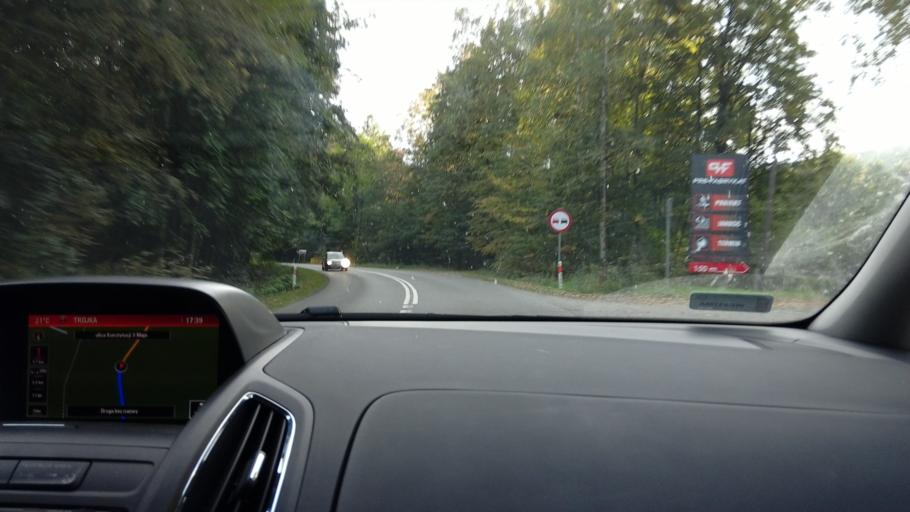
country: PL
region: Lower Silesian Voivodeship
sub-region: Powiat jeleniogorski
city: Karpacz
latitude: 50.7986
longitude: 15.7628
